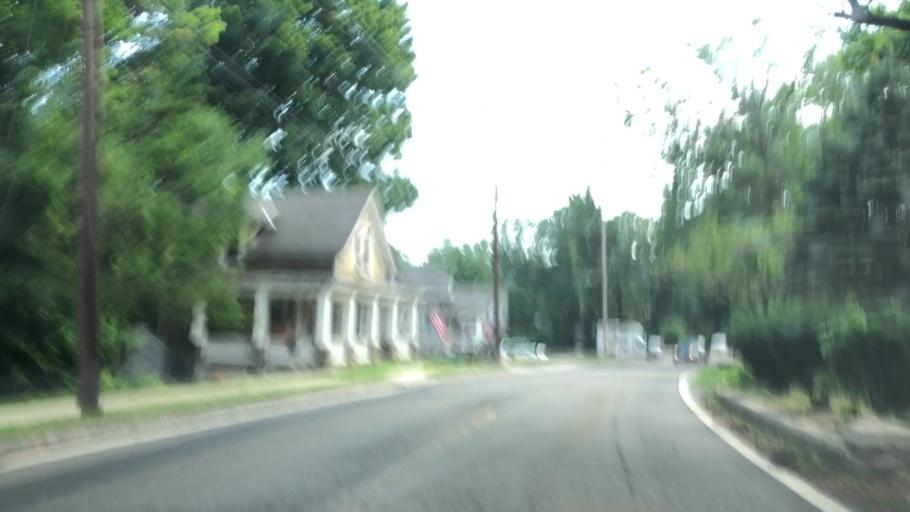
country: US
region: New Jersey
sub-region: Morris County
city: Mount Arlington
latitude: 40.9272
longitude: -74.6350
